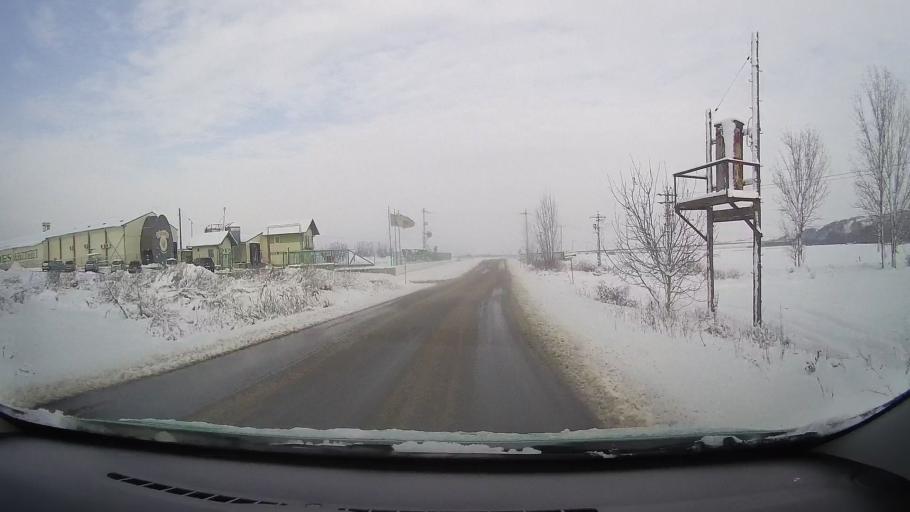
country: RO
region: Alba
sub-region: Comuna Pianu
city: Pianu de Jos
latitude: 45.9592
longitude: 23.4765
